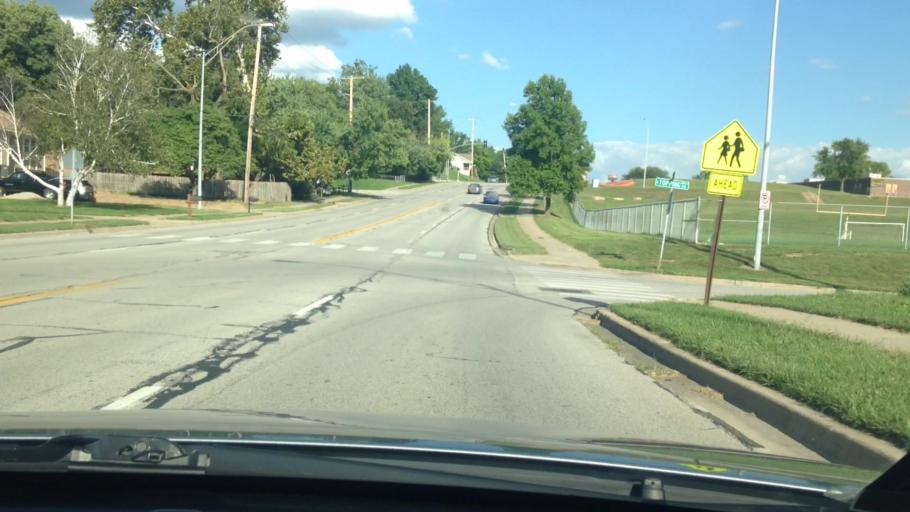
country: US
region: Missouri
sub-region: Clay County
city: Claycomo
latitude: 39.1806
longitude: -94.5124
